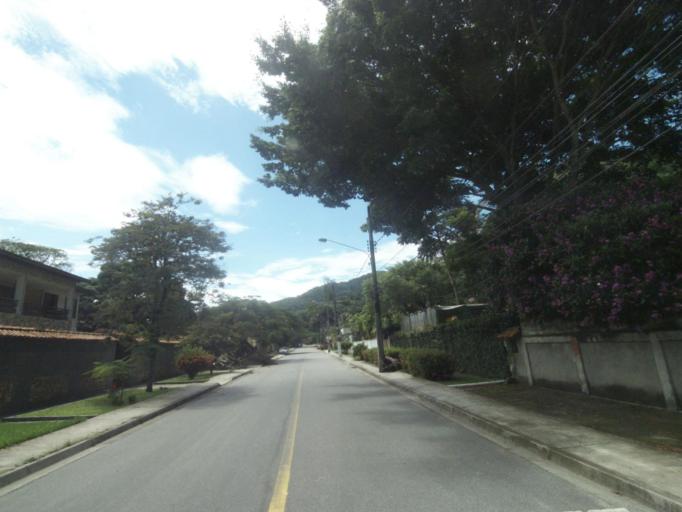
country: BR
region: Rio de Janeiro
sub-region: Niteroi
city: Niteroi
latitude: -22.9565
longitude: -43.0259
